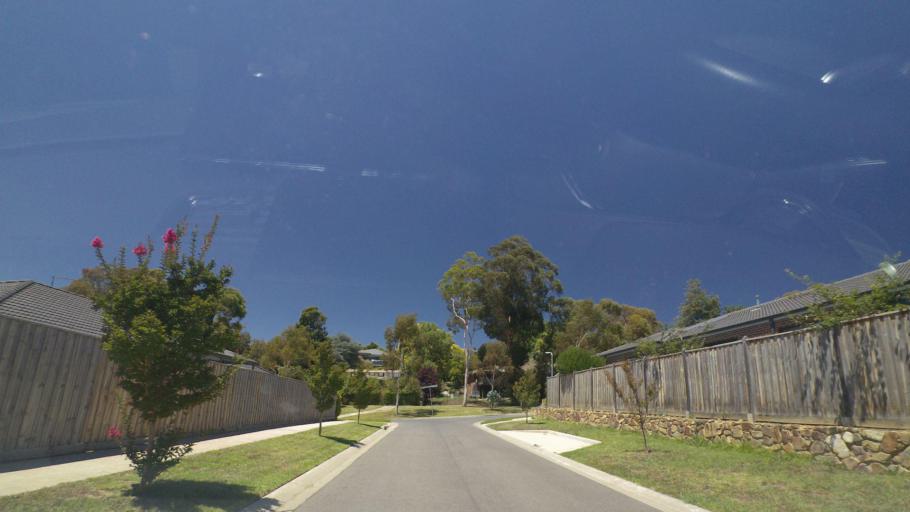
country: AU
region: Victoria
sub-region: Yarra Ranges
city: Lilydale
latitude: -37.7535
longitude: 145.3296
